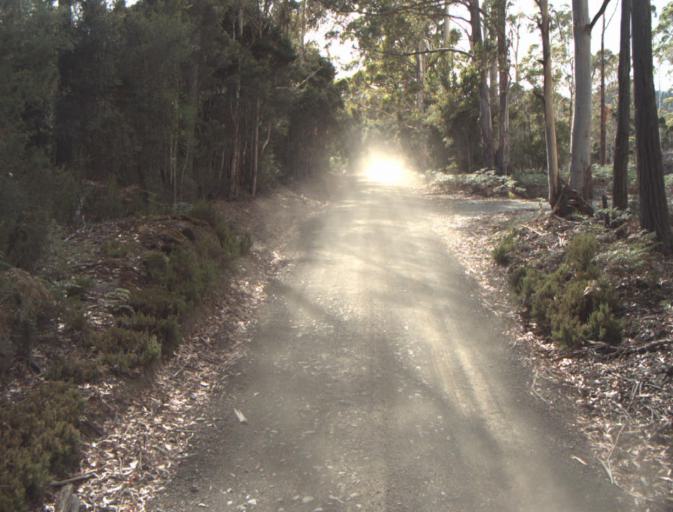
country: AU
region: Tasmania
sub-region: Launceston
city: Mayfield
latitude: -41.2625
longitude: 147.2498
